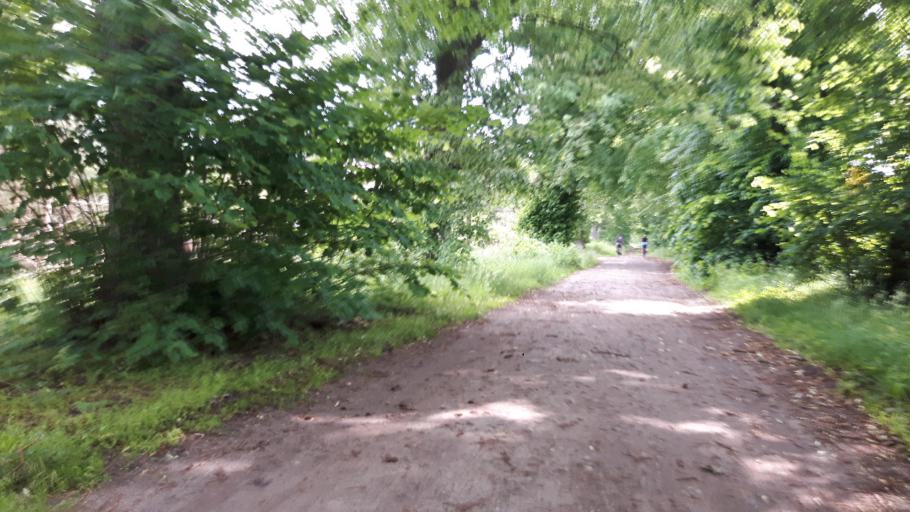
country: PL
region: Pomeranian Voivodeship
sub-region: Powiat leborski
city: Leba
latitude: 54.7541
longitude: 17.6188
